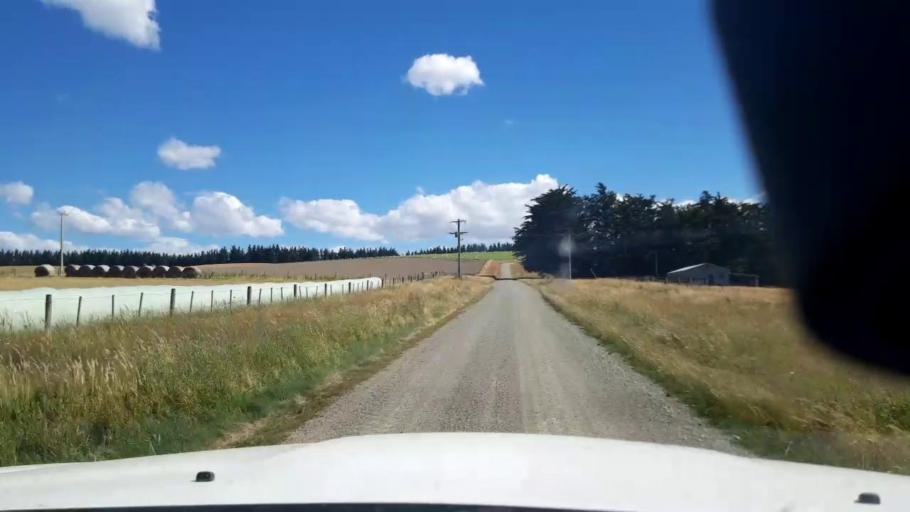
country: NZ
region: Canterbury
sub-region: Timaru District
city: Pleasant Point
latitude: -44.3162
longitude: 170.8881
